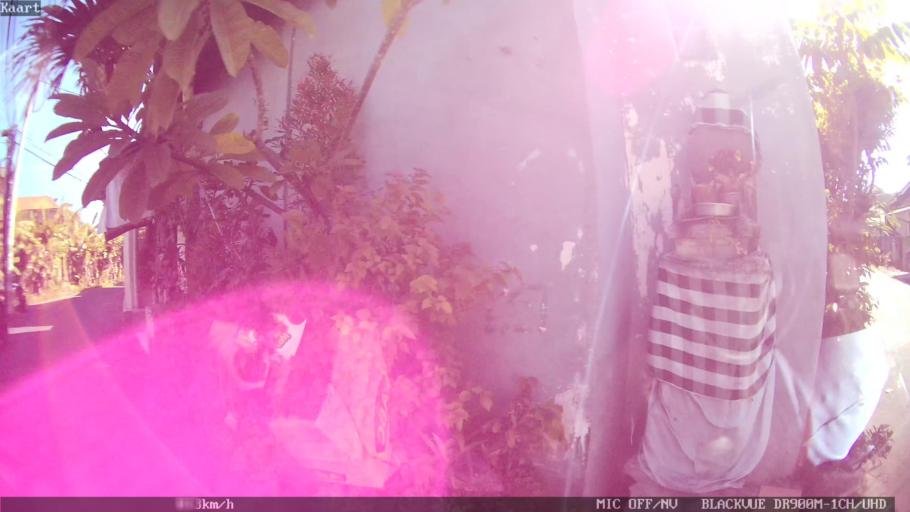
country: ID
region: Bali
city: Banjar Karangsuling
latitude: -8.6230
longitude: 115.1796
